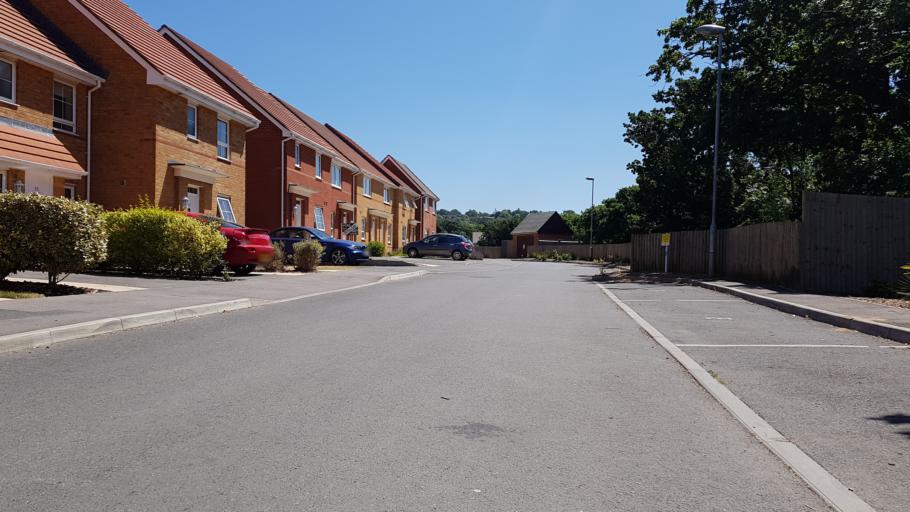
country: GB
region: England
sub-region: Isle of Wight
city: Newport
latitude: 50.6982
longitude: -1.2795
